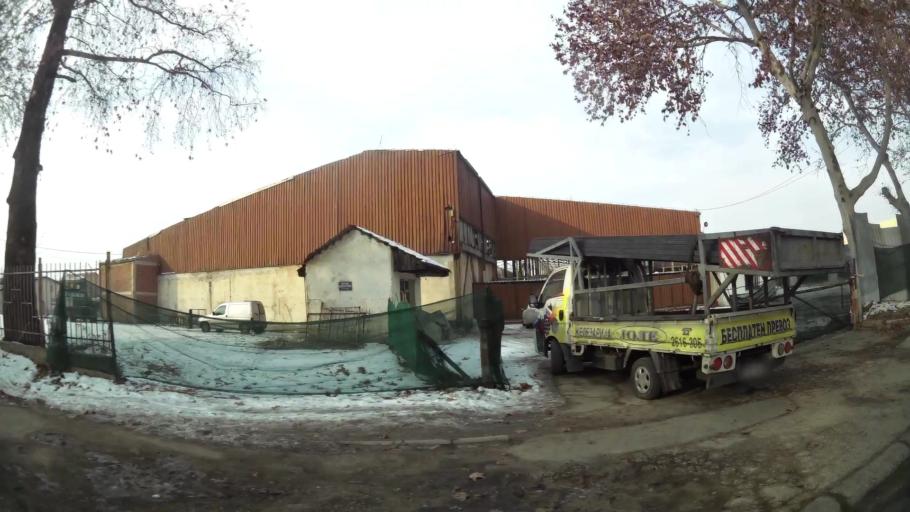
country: MK
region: Cair
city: Cair
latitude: 42.0242
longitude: 21.4300
